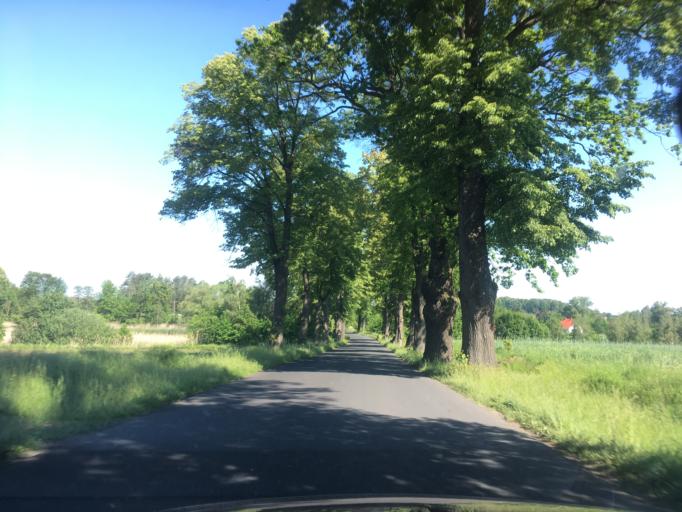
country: PL
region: Lower Silesian Voivodeship
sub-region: Powiat zgorzelecki
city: Sulikow
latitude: 51.1070
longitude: 15.0353
